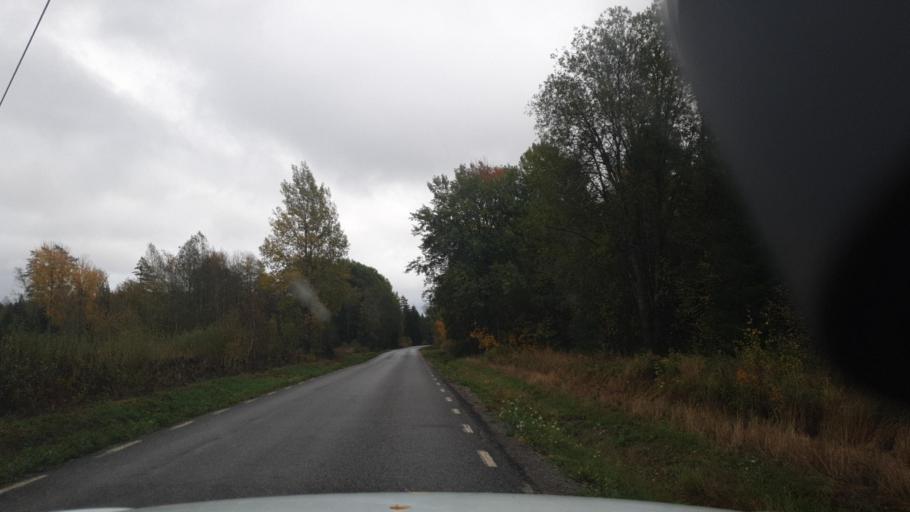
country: SE
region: Vaermland
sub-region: Karlstads Kommun
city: Valberg
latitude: 59.4134
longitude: 13.1650
